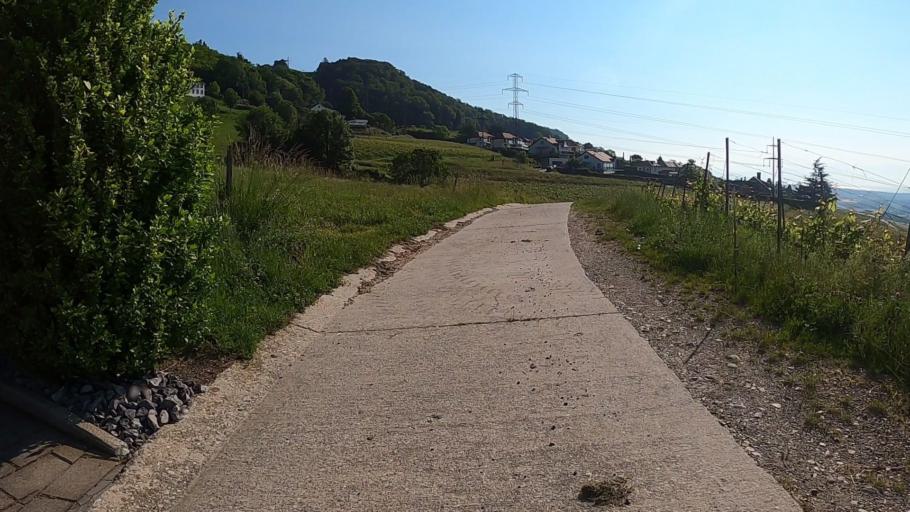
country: CH
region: Vaud
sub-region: Nyon District
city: Rolle
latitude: 46.4744
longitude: 6.3310
